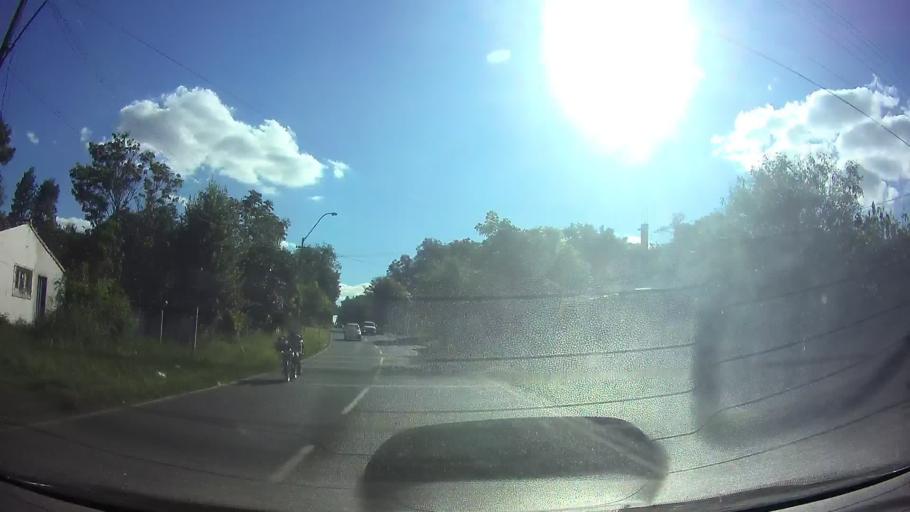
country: PY
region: Cordillera
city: Caacupe
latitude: -25.3902
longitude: -57.1387
